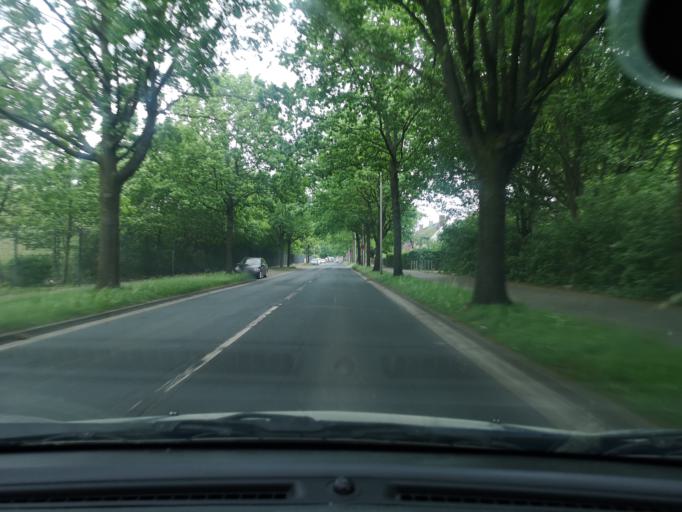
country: DE
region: Lower Saxony
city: Langenhagen
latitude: 52.4167
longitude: 9.6833
